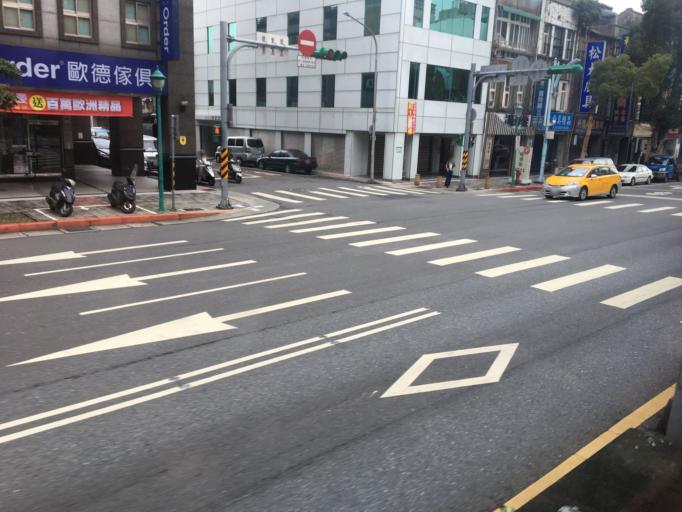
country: TW
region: Taipei
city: Taipei
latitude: 25.0670
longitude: 121.5138
